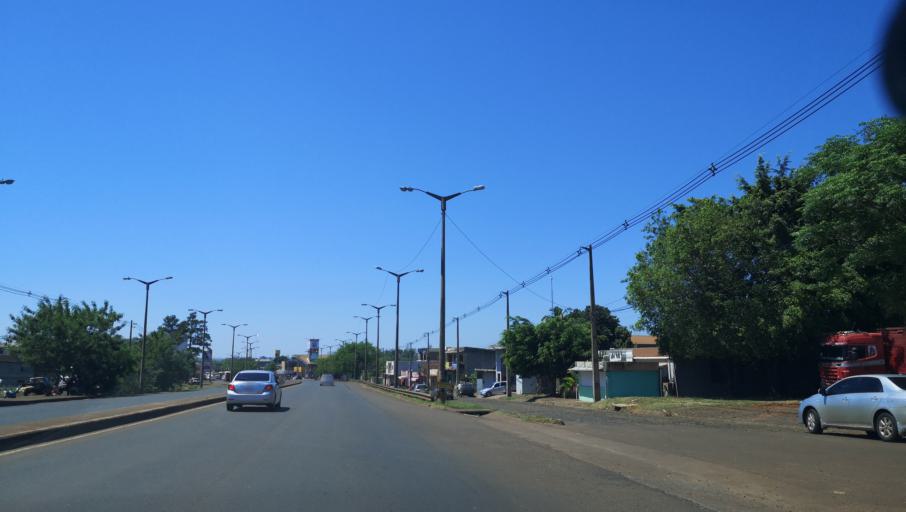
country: PY
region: Itapua
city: Encarnacion
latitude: -27.3100
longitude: -55.8864
